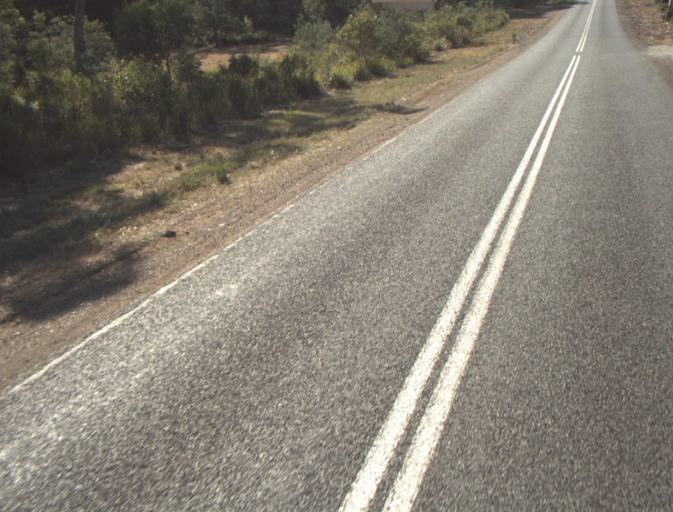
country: AU
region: Tasmania
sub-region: Launceston
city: Mayfield
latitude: -41.3026
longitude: 147.1334
